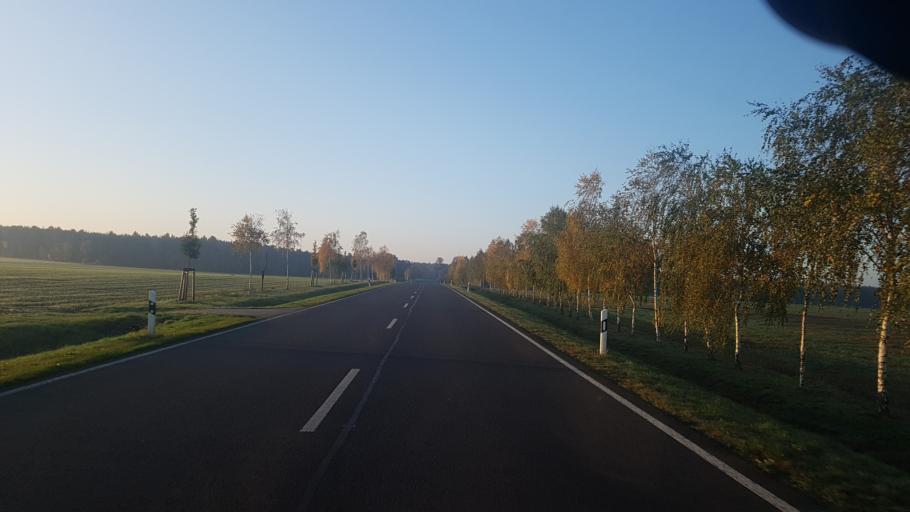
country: DE
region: Saxony
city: Schildau
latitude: 51.4864
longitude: 12.9869
